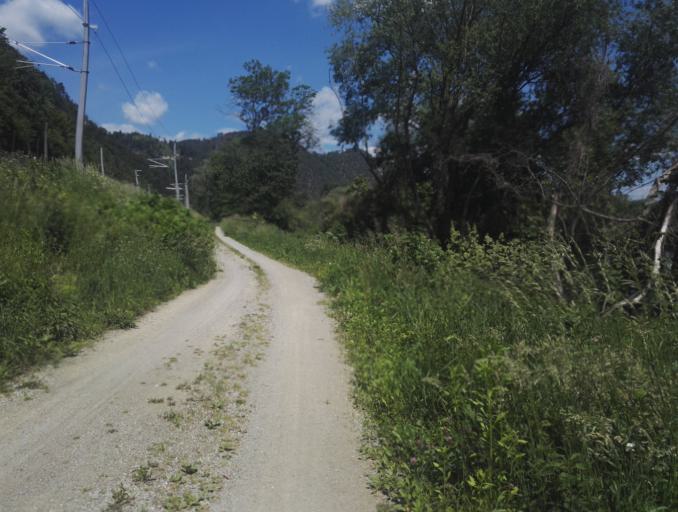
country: AT
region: Styria
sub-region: Politischer Bezirk Graz-Umgebung
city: Gratkorn
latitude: 47.1495
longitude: 15.3240
